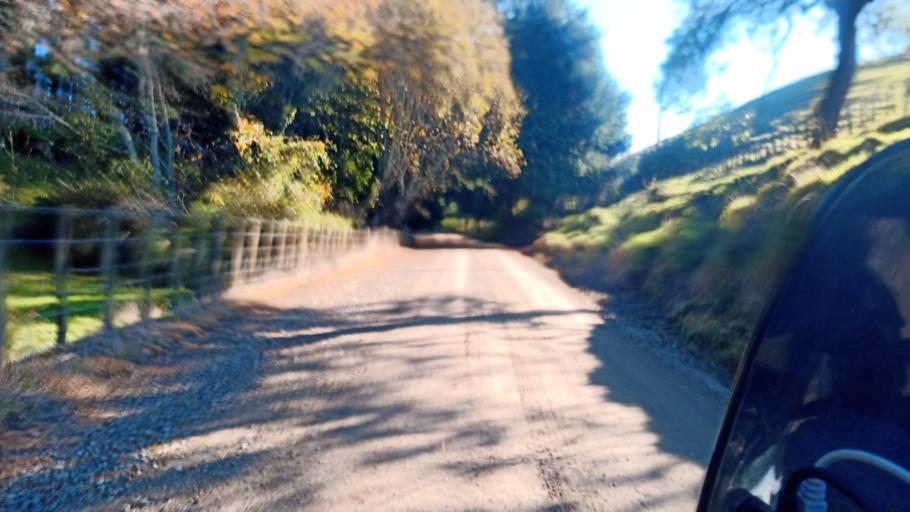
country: NZ
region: Hawke's Bay
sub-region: Wairoa District
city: Wairoa
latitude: -38.7816
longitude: 177.2683
